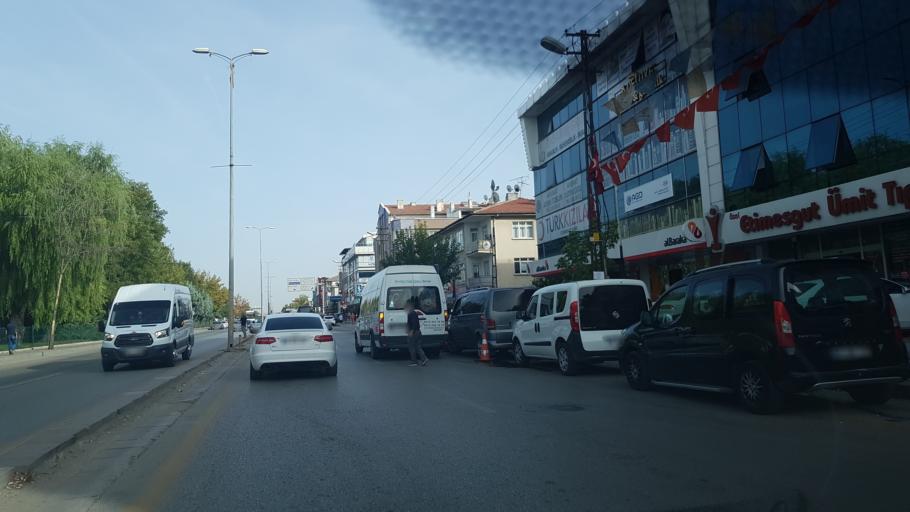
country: TR
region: Ankara
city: Etimesgut
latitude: 39.9493
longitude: 32.6595
